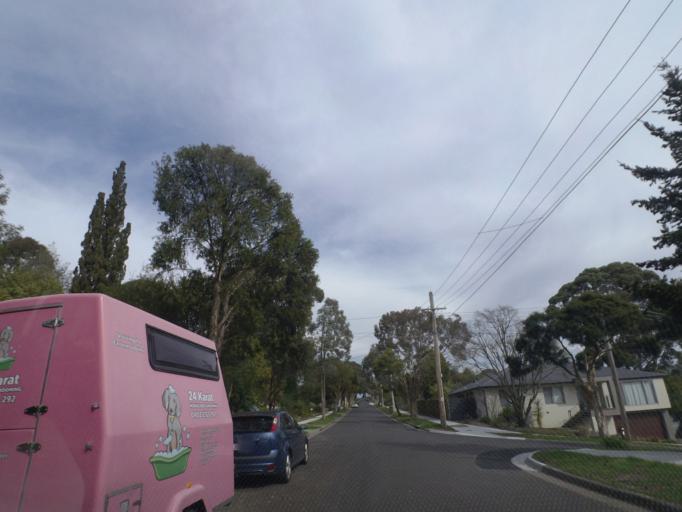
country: AU
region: Victoria
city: Mitcham
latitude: -37.8087
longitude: 145.2038
